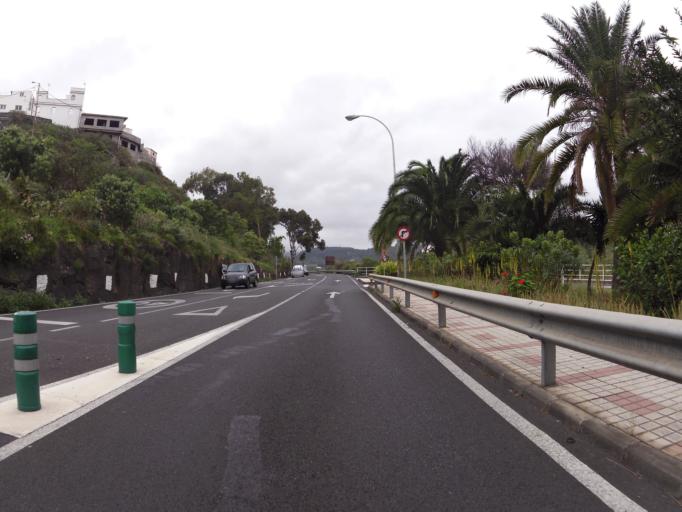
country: ES
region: Canary Islands
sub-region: Provincia de Las Palmas
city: Arucas
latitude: 28.0951
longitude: -15.4974
